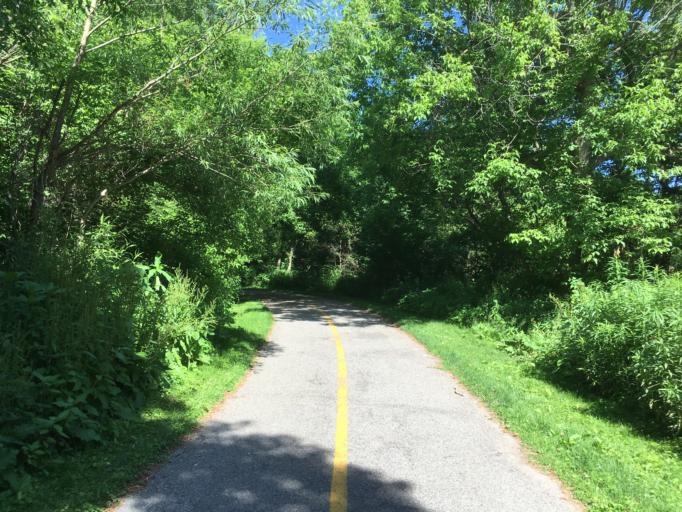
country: CA
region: Ontario
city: Oshawa
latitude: 43.8766
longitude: -78.8561
